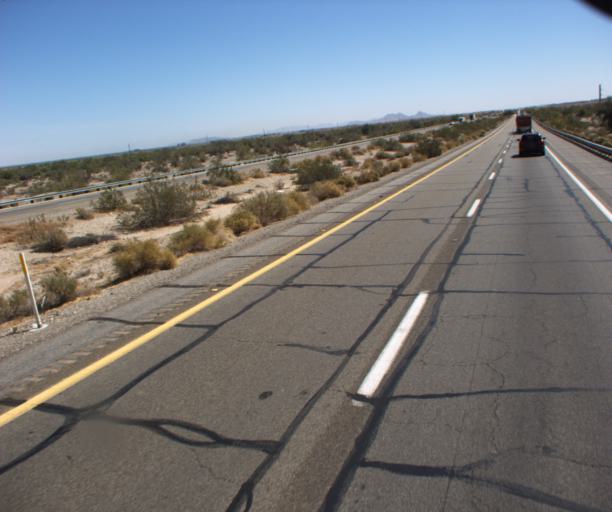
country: US
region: Arizona
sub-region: Yuma County
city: Wellton
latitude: 32.6608
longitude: -114.2589
